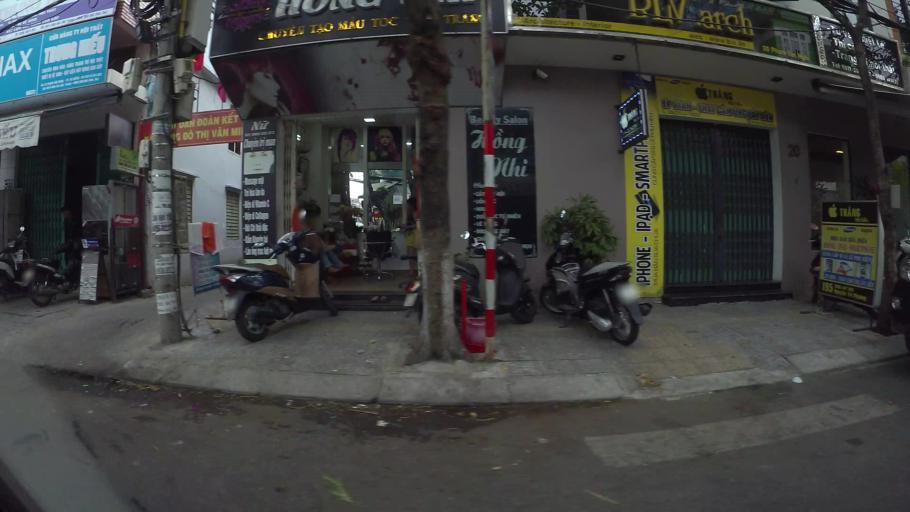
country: VN
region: Da Nang
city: Da Nang
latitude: 16.0586
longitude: 108.2095
